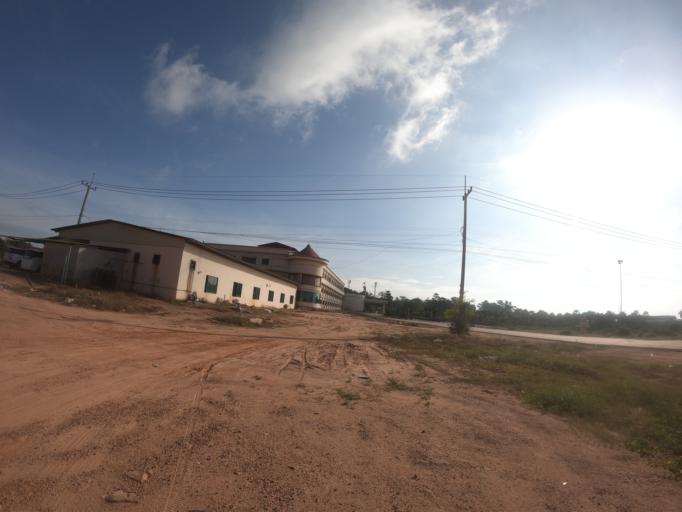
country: TH
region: Surin
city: Kap Choeng
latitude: 14.4327
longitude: 103.6978
